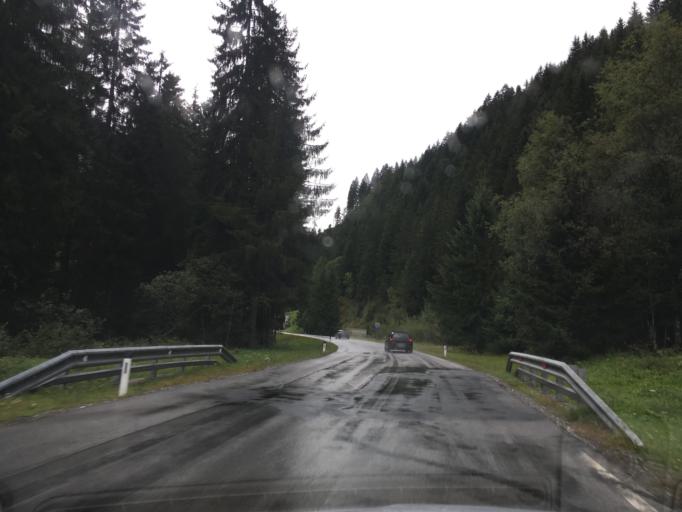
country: AT
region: Tyrol
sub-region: Politischer Bezirk Lienz
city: Hopfgarten in Defereggen
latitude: 46.9263
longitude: 12.4658
